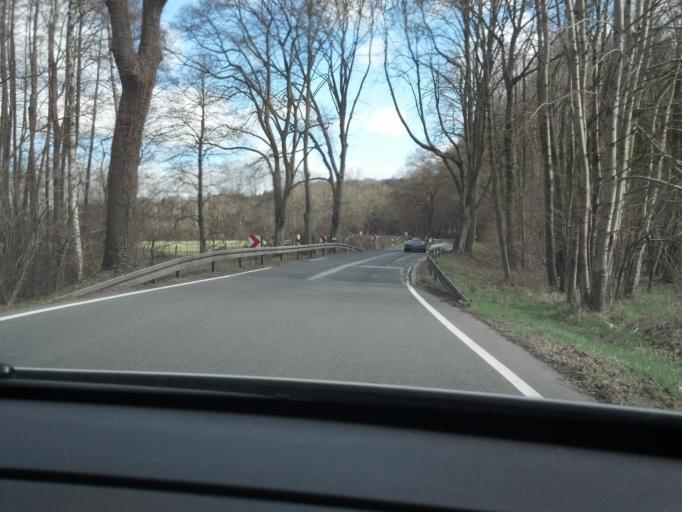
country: DE
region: Schleswig-Holstein
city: Langenlehsten
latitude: 53.4607
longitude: 10.7804
